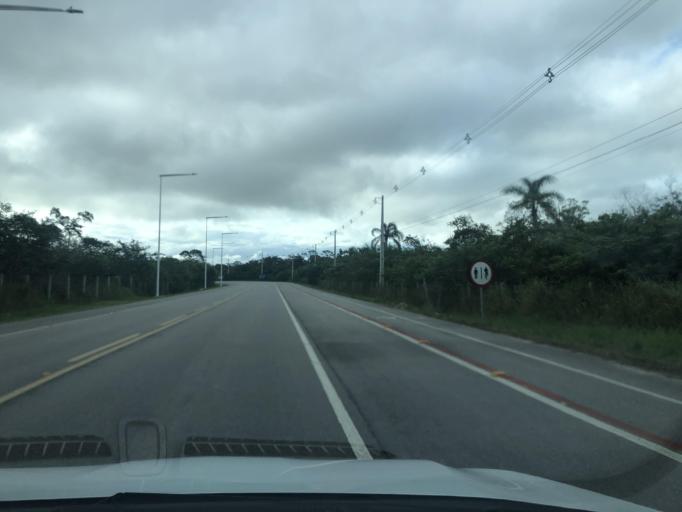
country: BR
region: Santa Catarina
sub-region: Florianopolis
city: Ribeirao da Ilha
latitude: -27.6826
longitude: -48.5292
